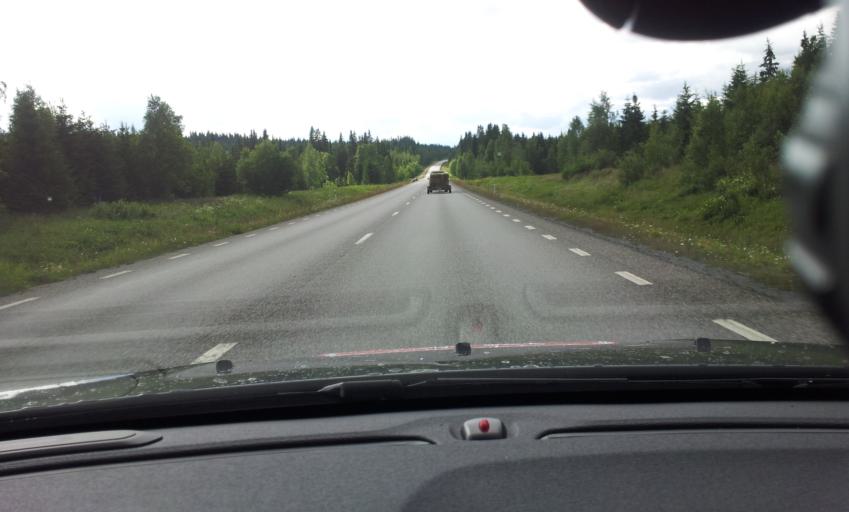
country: SE
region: Jaemtland
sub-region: Krokoms Kommun
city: Valla
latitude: 63.3118
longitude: 13.7507
